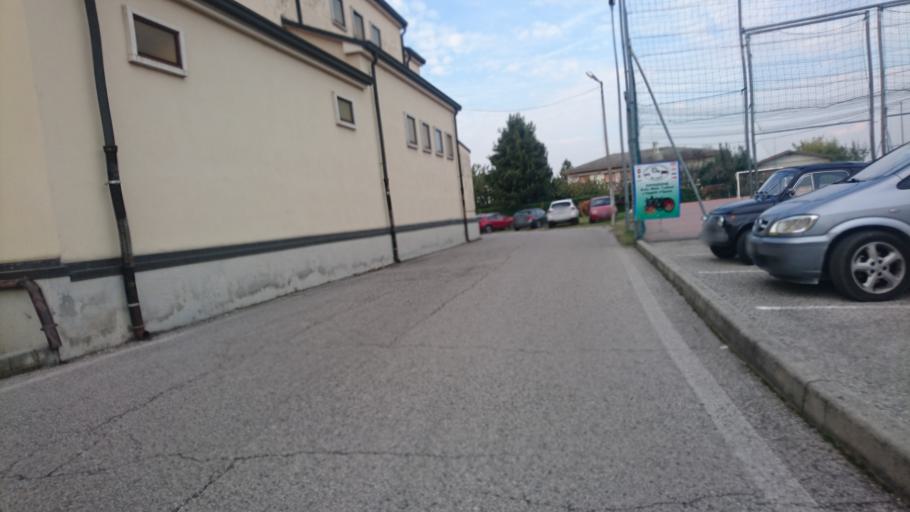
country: IT
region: Veneto
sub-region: Provincia di Padova
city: Gazzo
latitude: 45.5799
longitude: 11.6815
